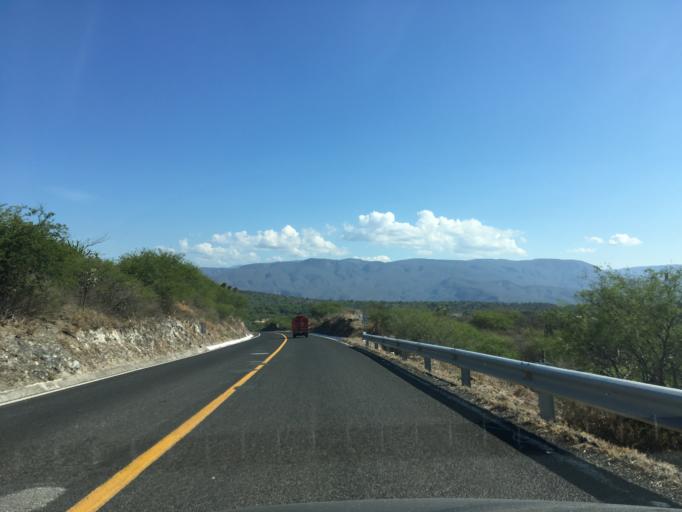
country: MX
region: Hidalgo
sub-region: San Agustin Metzquititlan
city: Mezquititlan
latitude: 20.4875
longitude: -98.6696
